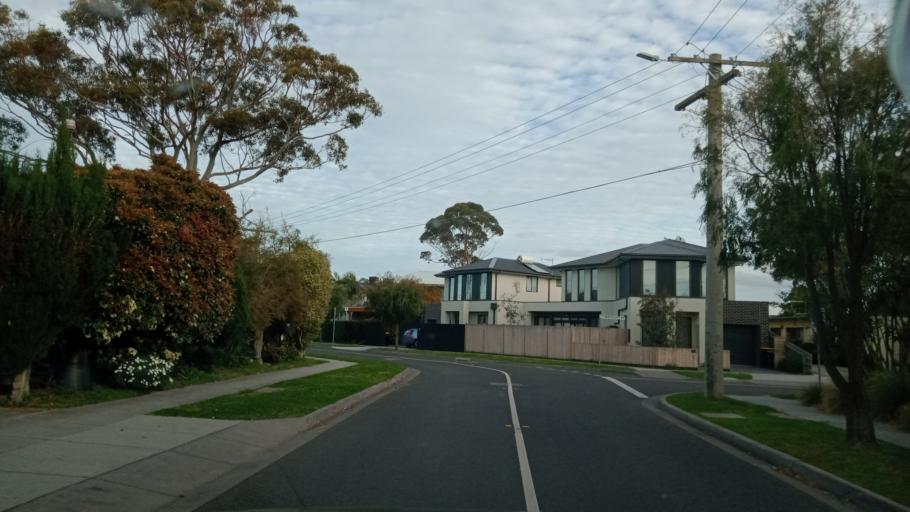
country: AU
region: Victoria
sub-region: Kingston
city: Chelsea
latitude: -38.0396
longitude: 145.1207
